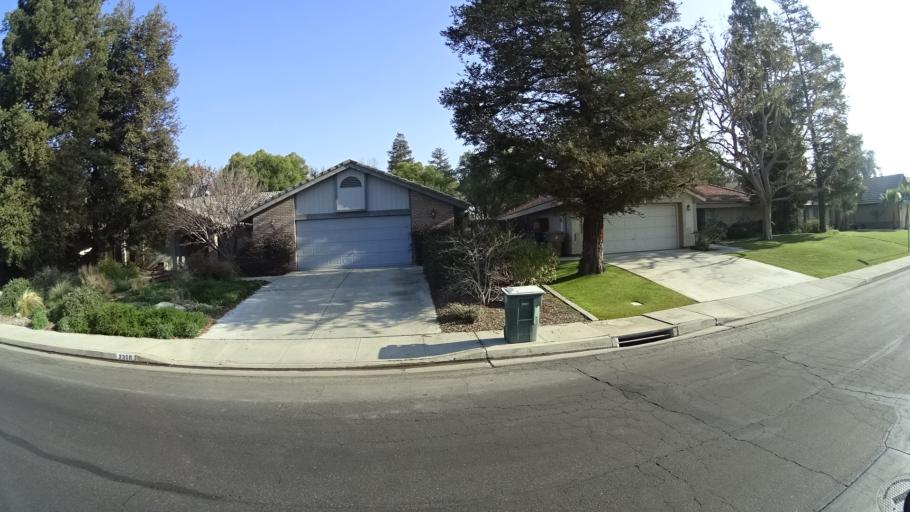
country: US
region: California
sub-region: Kern County
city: Greenacres
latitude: 35.3338
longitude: -119.1065
